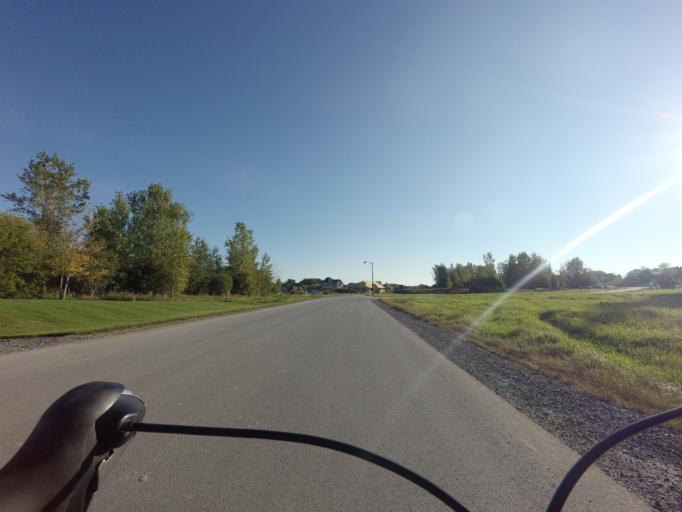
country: CA
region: Ontario
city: Bells Corners
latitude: 45.2139
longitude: -75.7033
